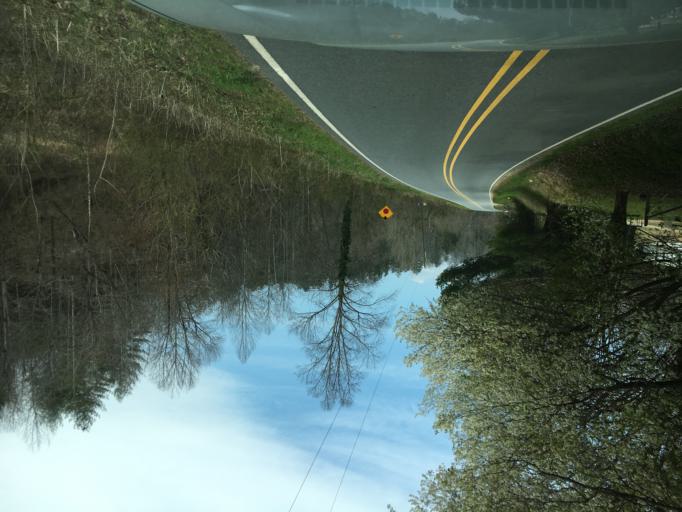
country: US
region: North Carolina
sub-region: Rutherford County
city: Lake Lure
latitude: 35.4199
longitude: -82.1763
